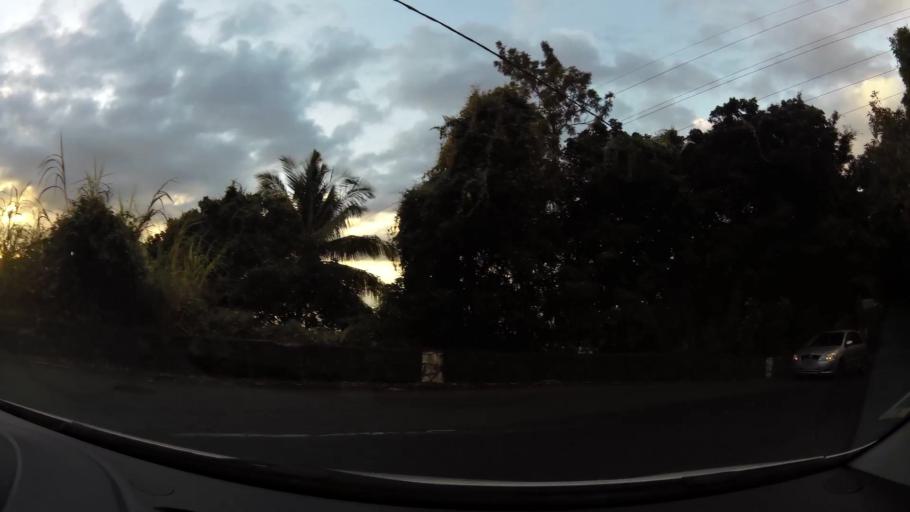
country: RE
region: Reunion
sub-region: Reunion
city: Saint-Denis
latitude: -20.9088
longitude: 55.4626
